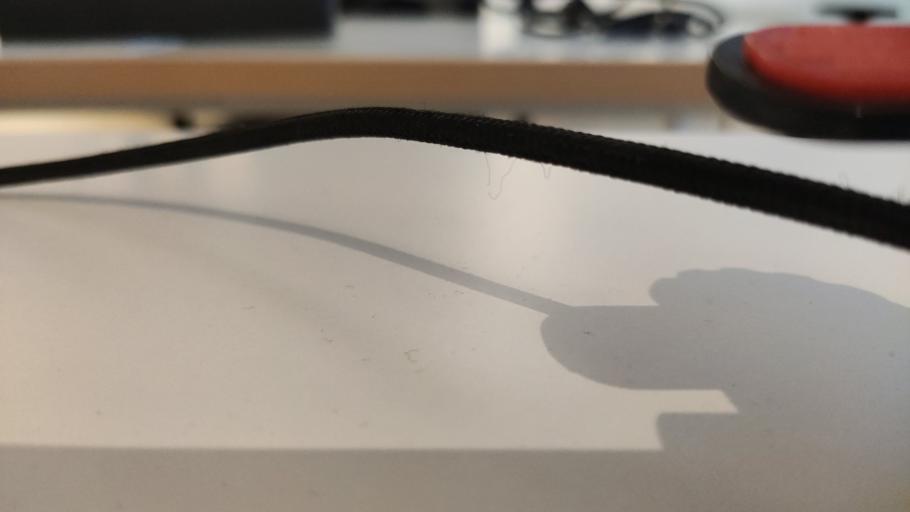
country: RU
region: Moskovskaya
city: Ruza
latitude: 55.7921
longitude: 36.2841
